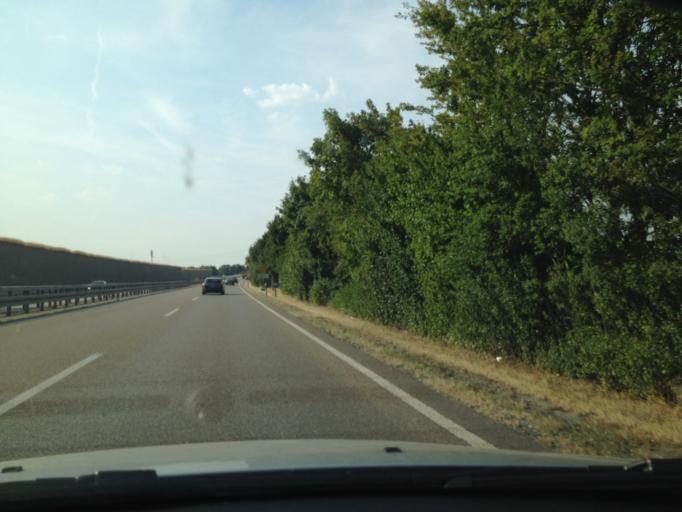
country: DE
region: Bavaria
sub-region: Swabia
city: Asbach-Baumenheim
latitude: 48.6873
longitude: 10.8182
